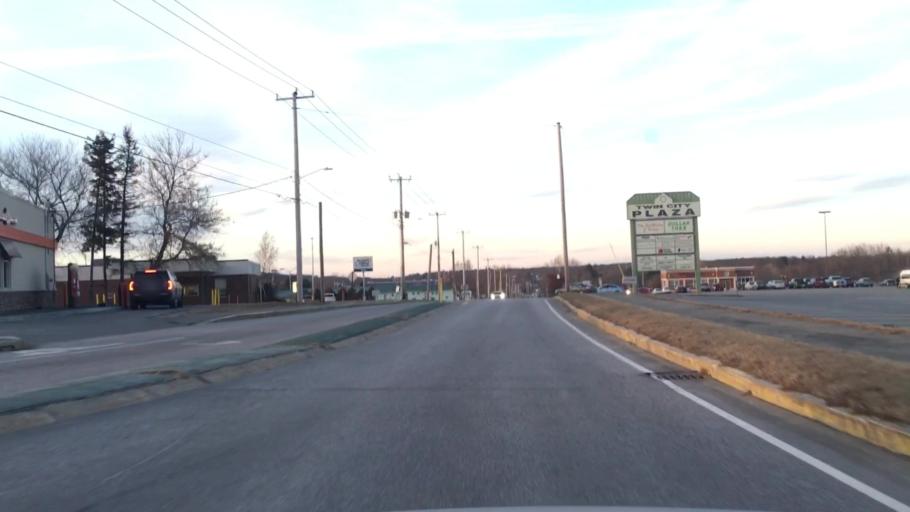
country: US
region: Maine
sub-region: Penobscot County
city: Brewer
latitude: 44.7851
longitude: -68.7526
